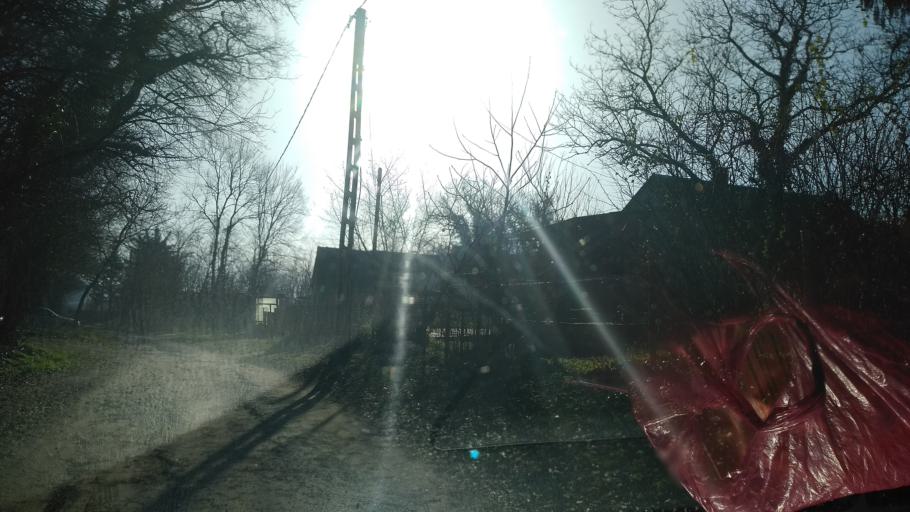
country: HU
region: Somogy
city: Barcs
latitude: 45.9535
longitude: 17.5088
